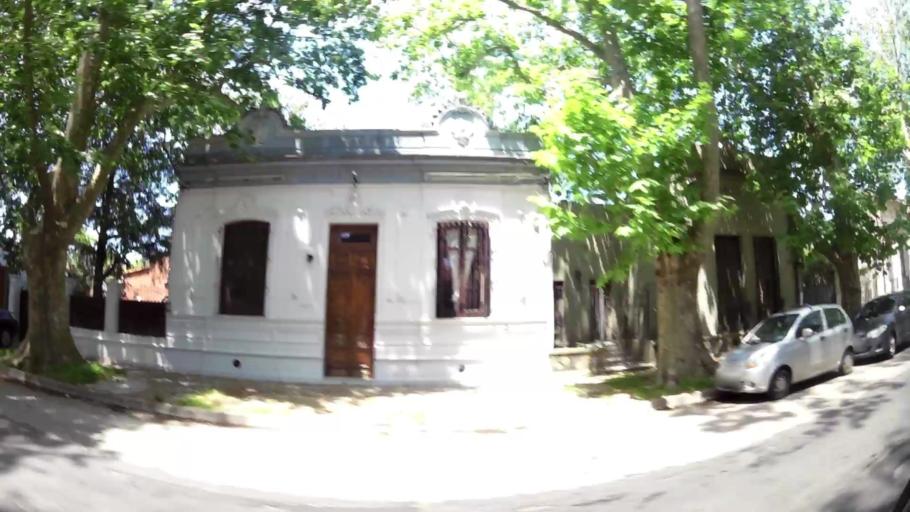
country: UY
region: Montevideo
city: Montevideo
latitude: -34.8679
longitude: -56.2043
